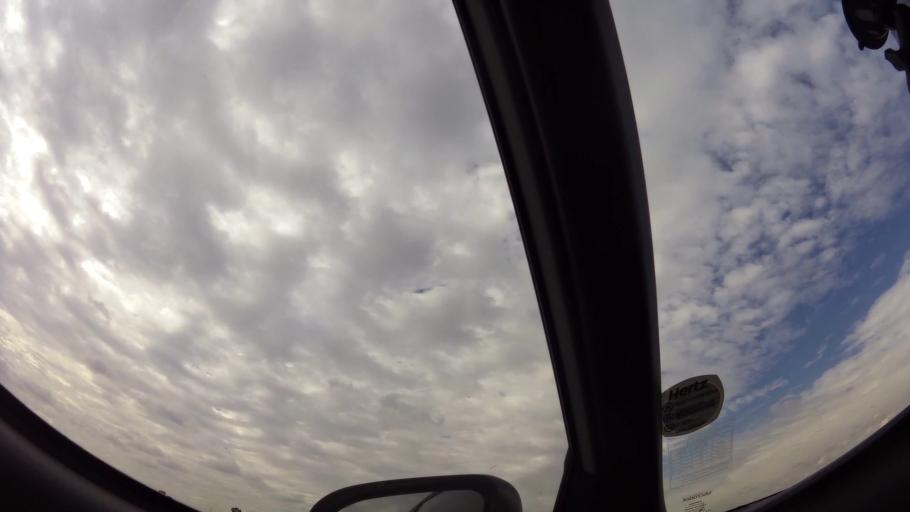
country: ZA
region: Gauteng
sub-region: Ekurhuleni Metropolitan Municipality
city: Germiston
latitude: -26.3005
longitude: 28.1643
